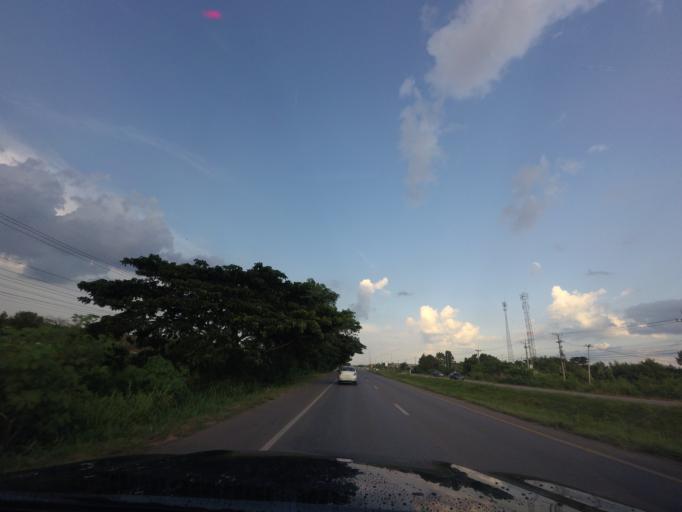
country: TH
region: Khon Kaen
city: Khon Kaen
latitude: 16.3949
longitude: 102.8541
